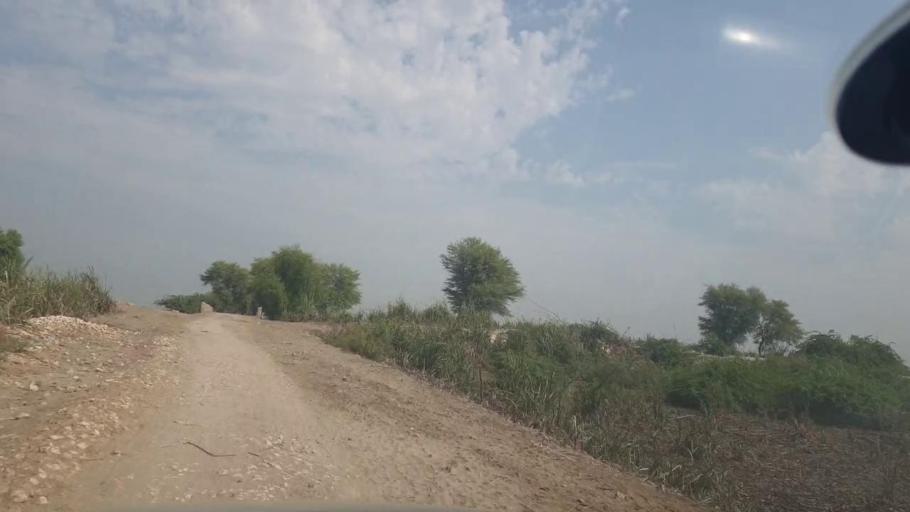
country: PK
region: Balochistan
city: Mehrabpur
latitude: 28.1169
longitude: 68.0914
